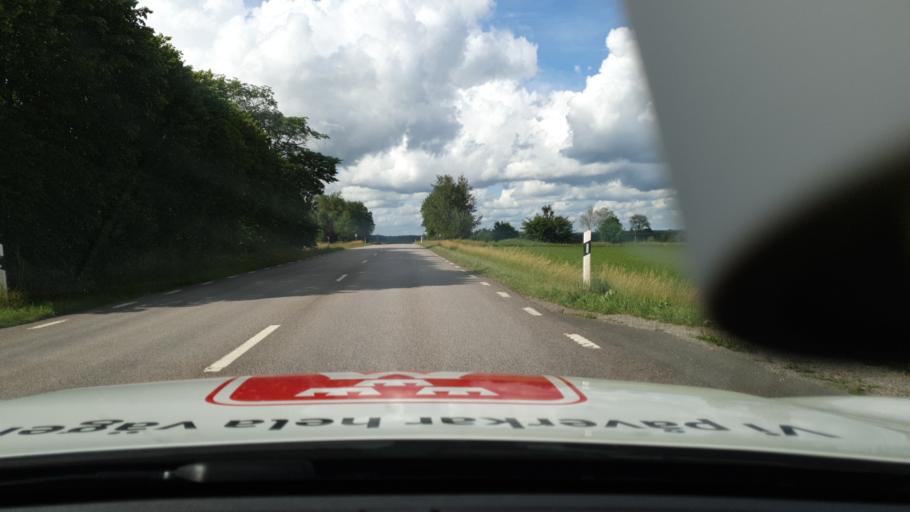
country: SE
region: Vaestra Goetaland
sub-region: Falkopings Kommun
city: Falkoeping
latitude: 58.1265
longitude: 13.5530
